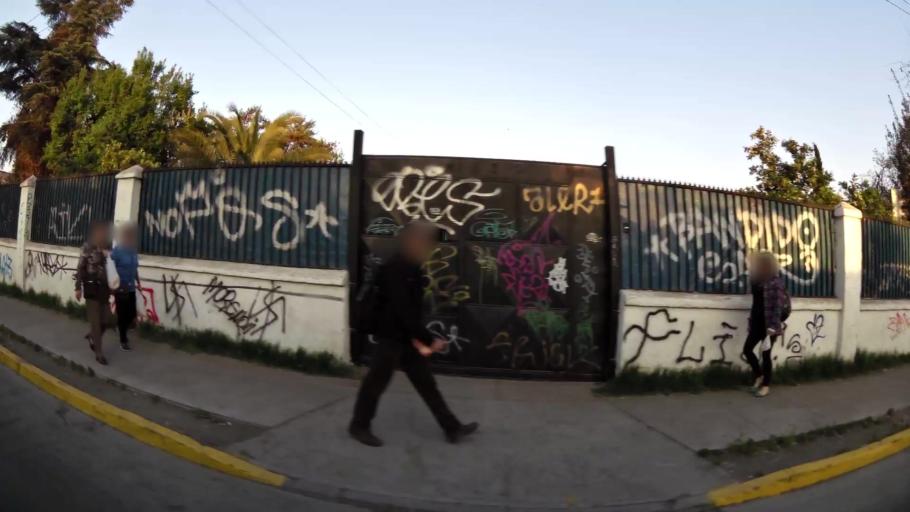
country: CL
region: Santiago Metropolitan
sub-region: Provincia de Santiago
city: La Pintana
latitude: -33.5483
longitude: -70.6672
